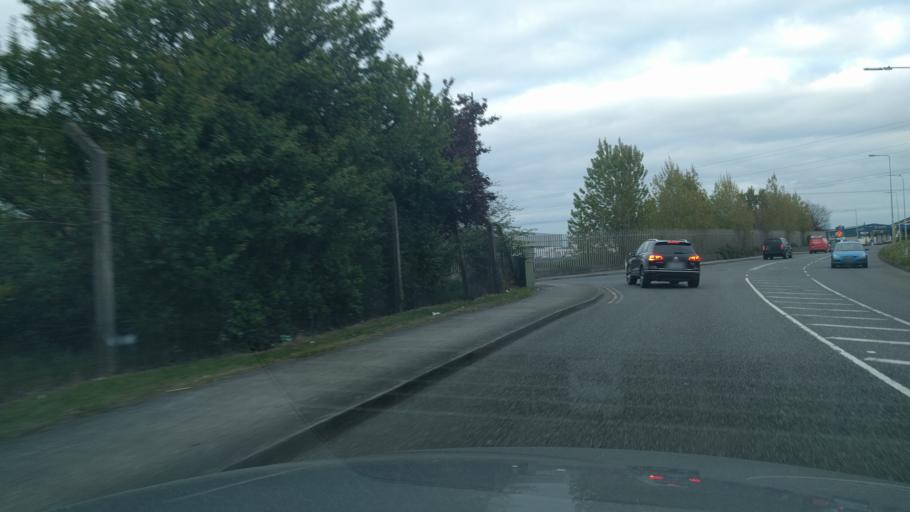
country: IE
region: Leinster
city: Crumlin
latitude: 53.3166
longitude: -6.3472
